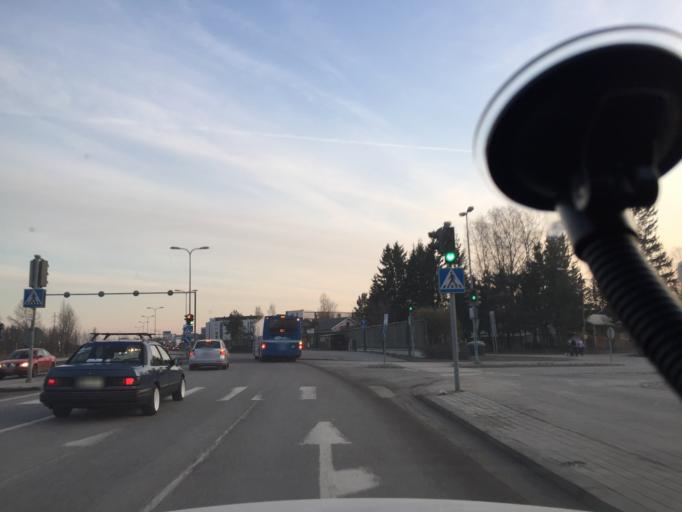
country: FI
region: Uusimaa
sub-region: Helsinki
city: Vantaa
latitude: 60.2728
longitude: 24.9696
